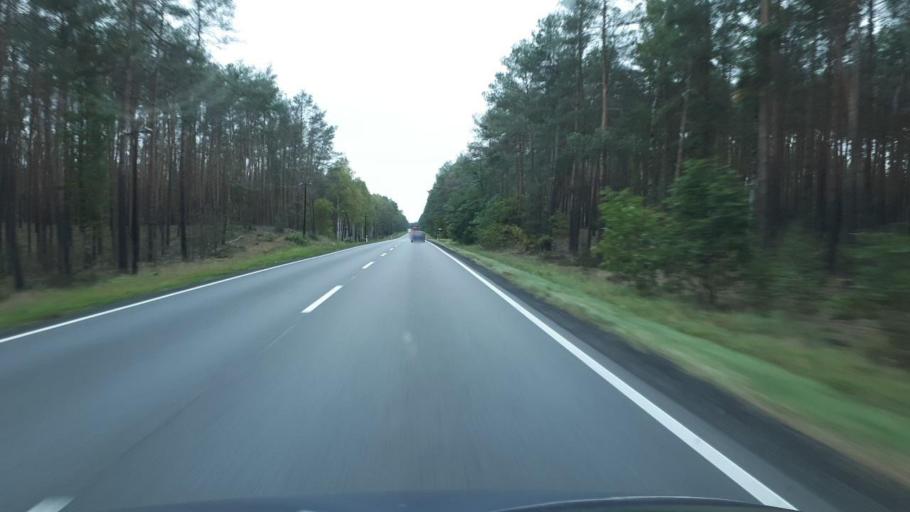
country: PL
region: Greater Poland Voivodeship
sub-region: Powiat ostrzeszowski
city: Ostrzeszow
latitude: 51.4665
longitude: 17.8960
